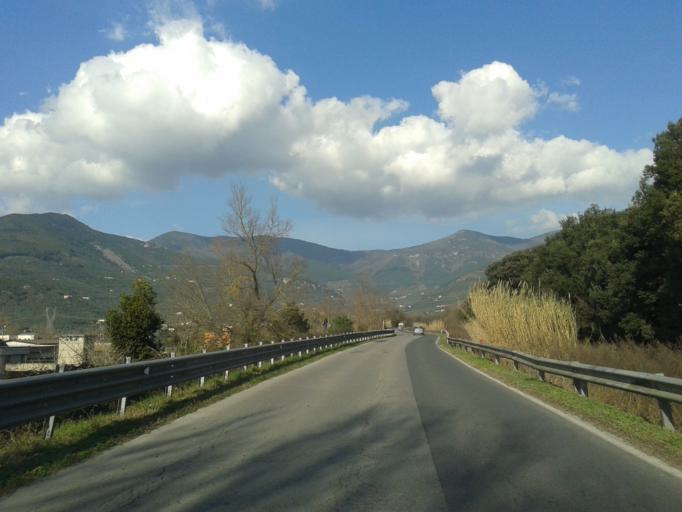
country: IT
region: Tuscany
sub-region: Province of Pisa
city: Gabella
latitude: 43.7117
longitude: 10.5071
